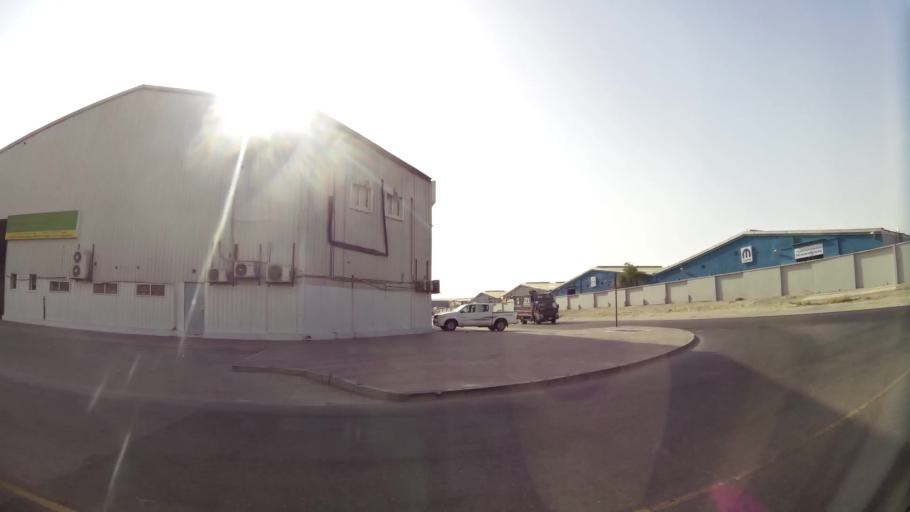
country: AE
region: Ash Shariqah
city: Sharjah
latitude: 25.2314
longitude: 55.3627
